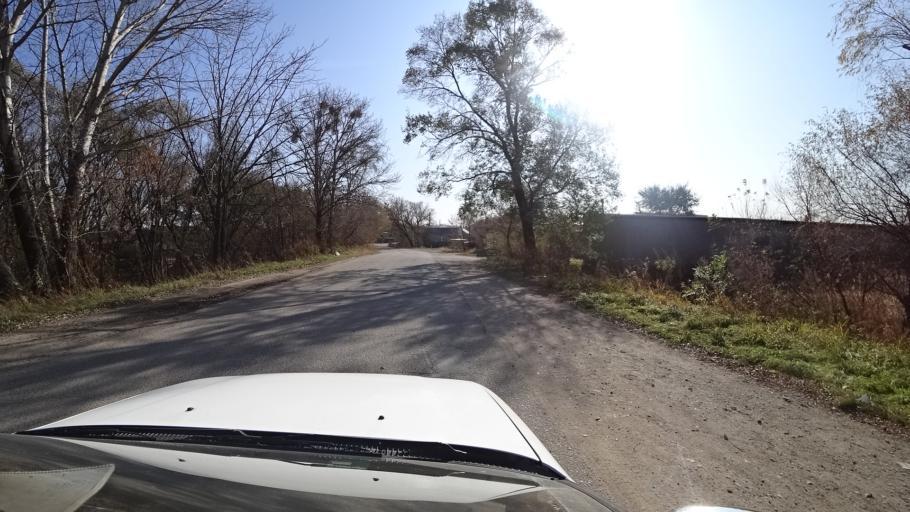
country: RU
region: Primorskiy
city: Dal'nerechensk
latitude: 45.9294
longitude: 133.7226
